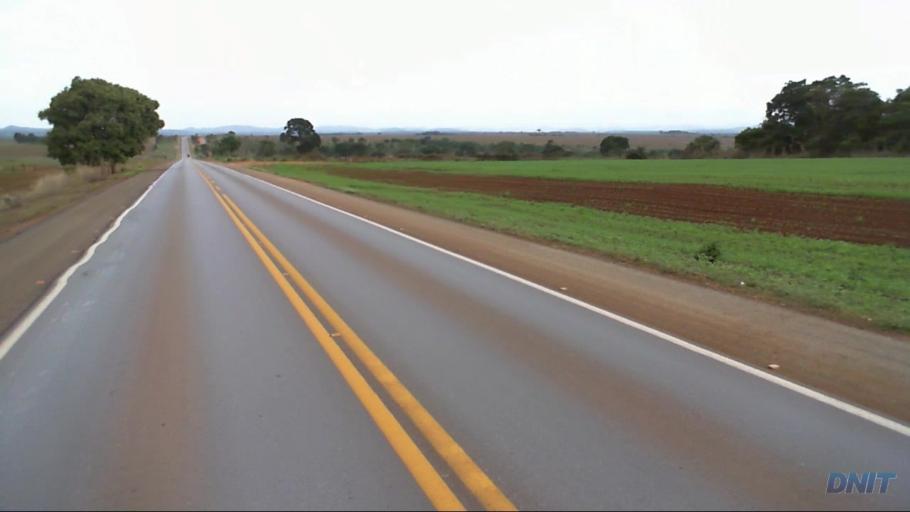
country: BR
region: Goias
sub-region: Uruacu
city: Uruacu
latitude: -14.6616
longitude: -49.1534
